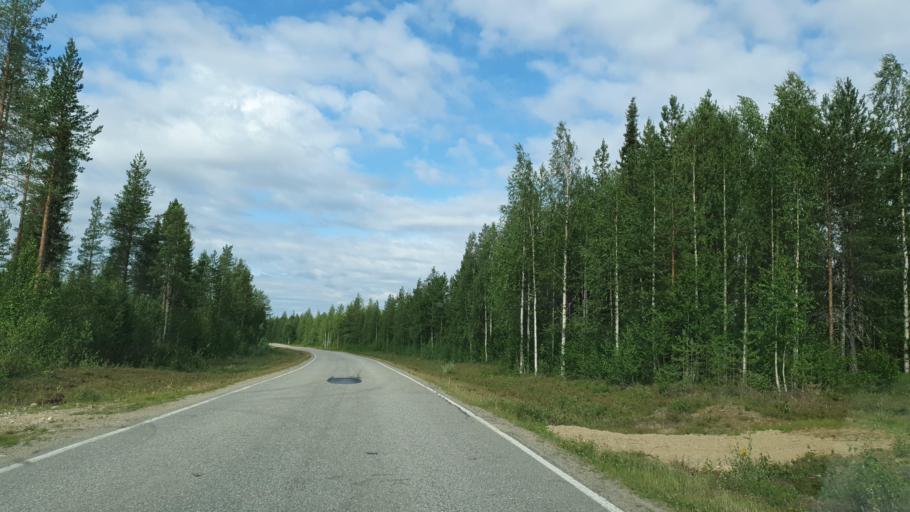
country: FI
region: Lapland
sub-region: Pohjois-Lappi
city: Sodankylae
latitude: 67.5242
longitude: 26.0152
